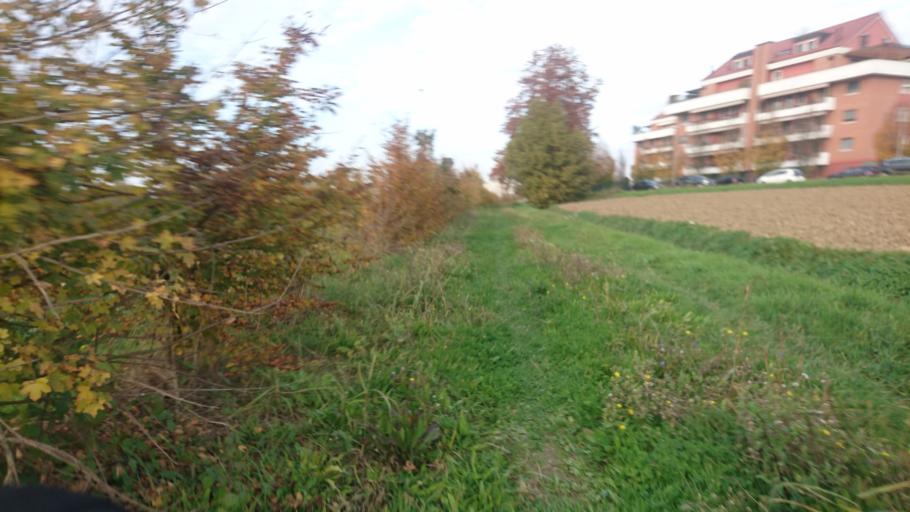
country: IT
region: Veneto
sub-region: Provincia di Padova
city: Mandriola-Sant'Agostino
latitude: 45.3826
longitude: 11.8455
